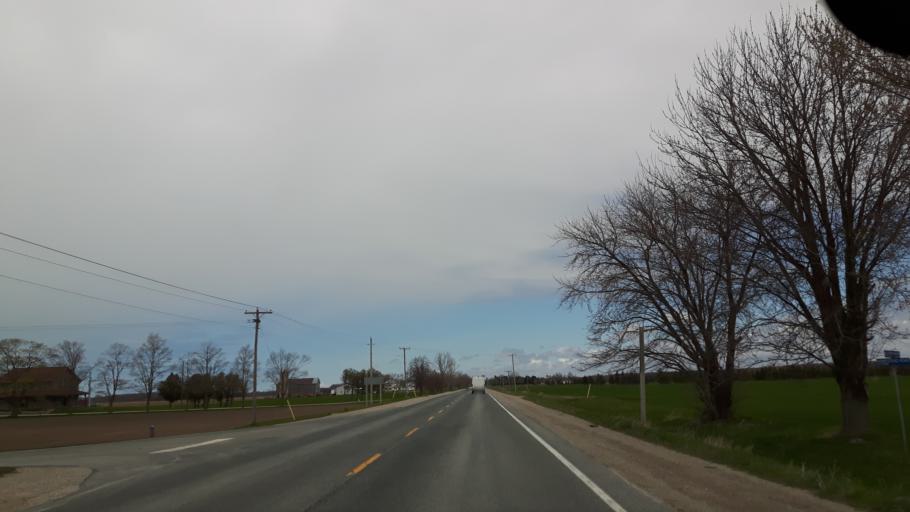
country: CA
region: Ontario
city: Bluewater
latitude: 43.4840
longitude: -81.6975
